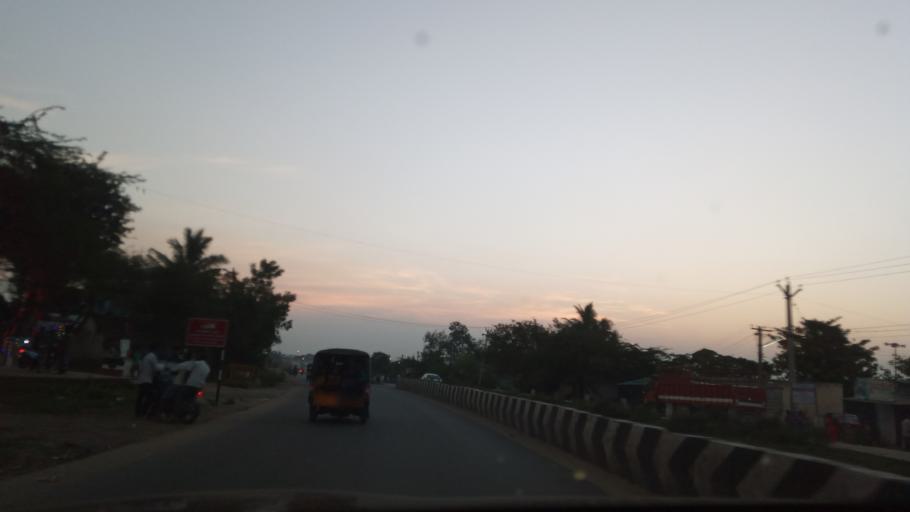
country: IN
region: Tamil Nadu
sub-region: Vellore
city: Walajapet
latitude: 12.9259
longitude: 79.3470
